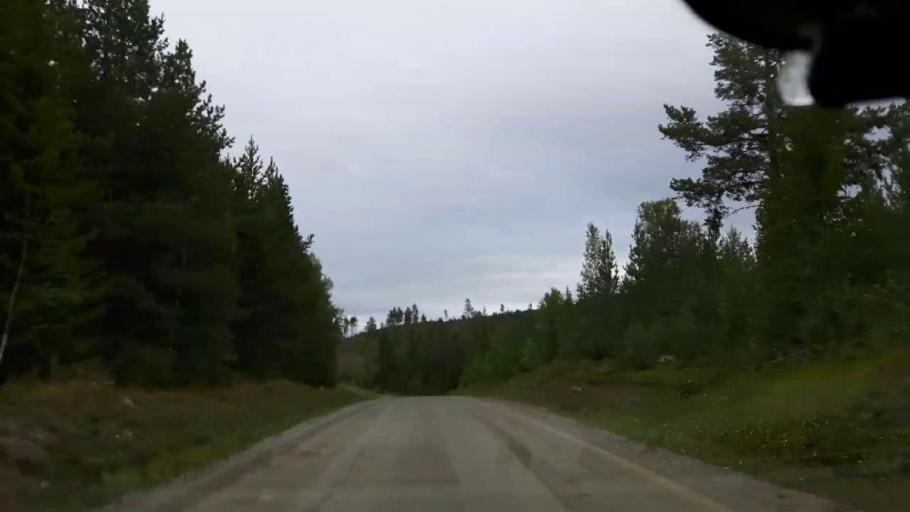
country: SE
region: Vaesternorrland
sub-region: Ange Kommun
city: Fransta
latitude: 62.8572
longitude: 16.0383
